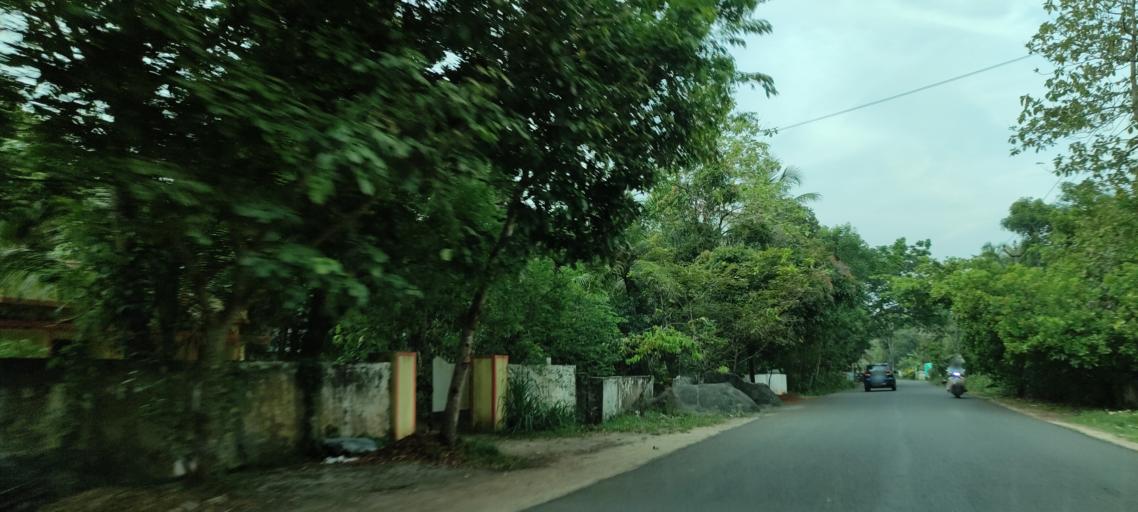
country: IN
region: Kerala
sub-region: Kottayam
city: Vaikam
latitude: 9.7328
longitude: 76.3621
